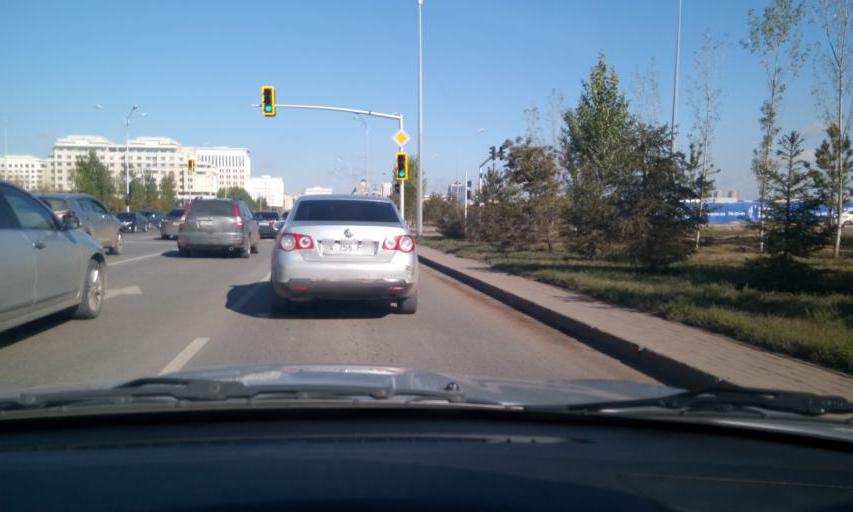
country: KZ
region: Astana Qalasy
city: Astana
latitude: 51.0994
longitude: 71.4285
